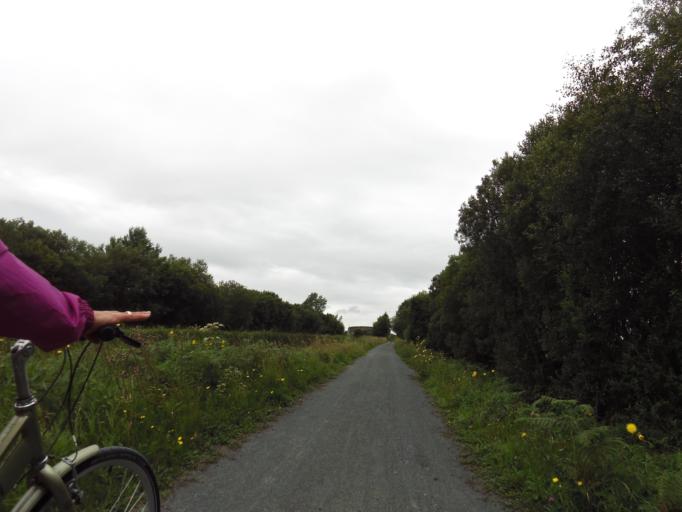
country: IE
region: Leinster
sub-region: An Iarmhi
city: Moate
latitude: 53.5855
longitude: -7.6224
